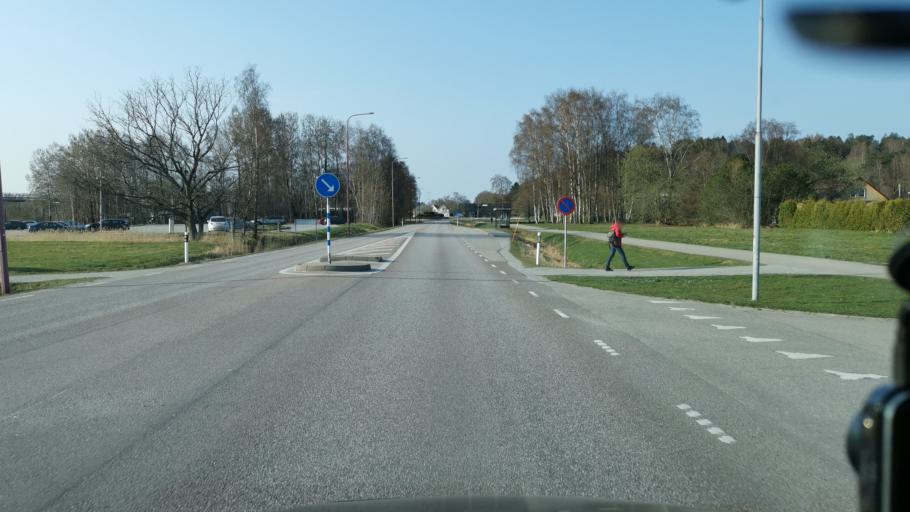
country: SE
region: Vaestra Goetaland
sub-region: Stenungsunds Kommun
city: Stora Hoga
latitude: 58.0195
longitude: 11.8354
